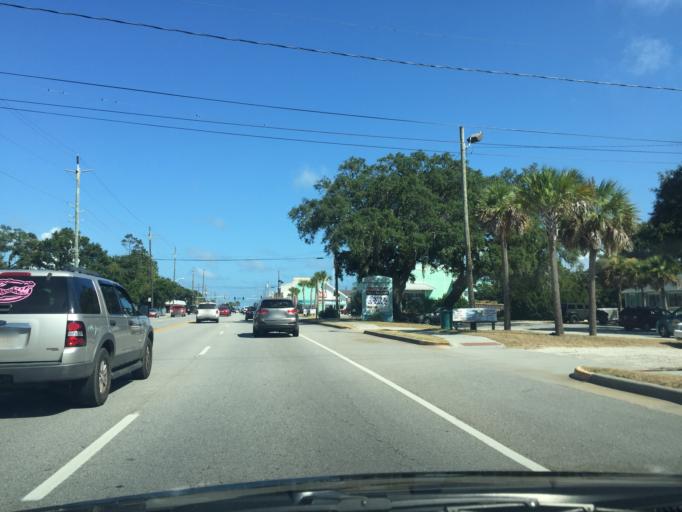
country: US
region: Georgia
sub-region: Chatham County
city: Tybee Island
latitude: 32.0137
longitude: -80.8457
